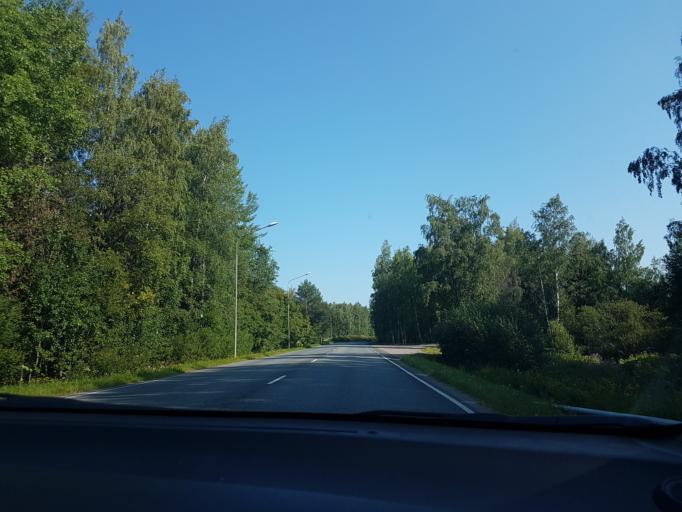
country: FI
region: Uusimaa
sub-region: Helsinki
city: Kerava
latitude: 60.3848
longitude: 25.0983
